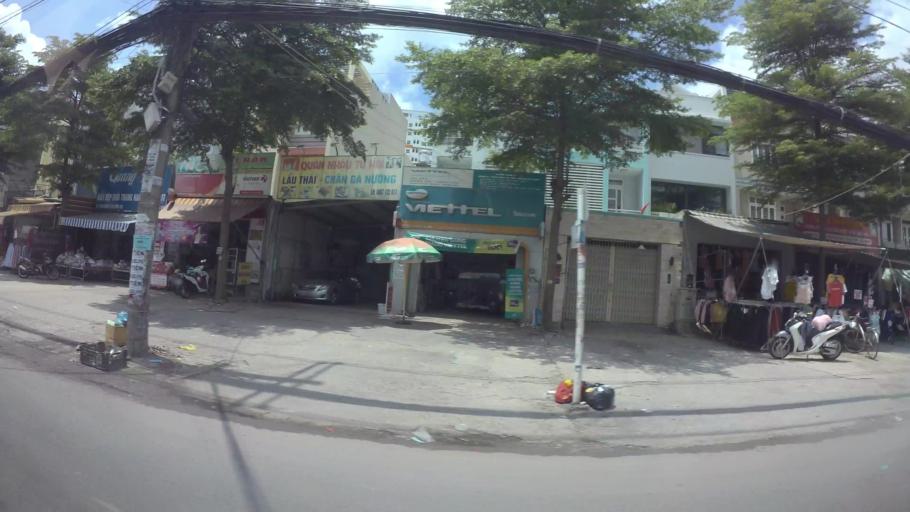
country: VN
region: Ho Chi Minh City
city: Quan Chin
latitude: 10.8290
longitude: 106.7731
